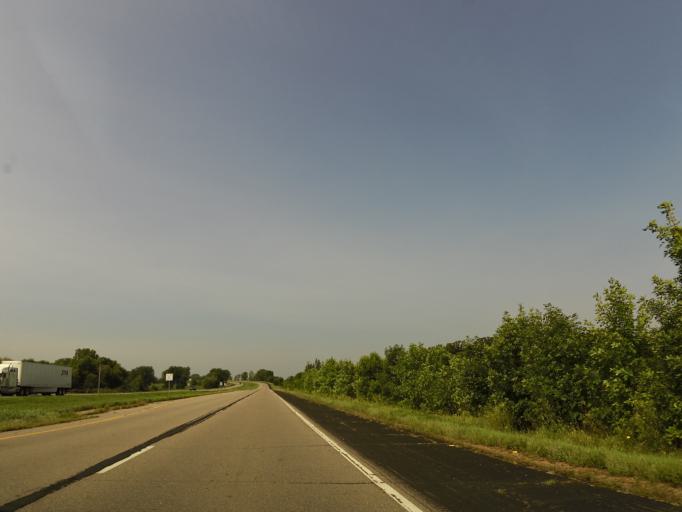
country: US
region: Minnesota
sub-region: Carver County
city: Norwood (historical)
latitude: 44.7721
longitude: -93.9407
